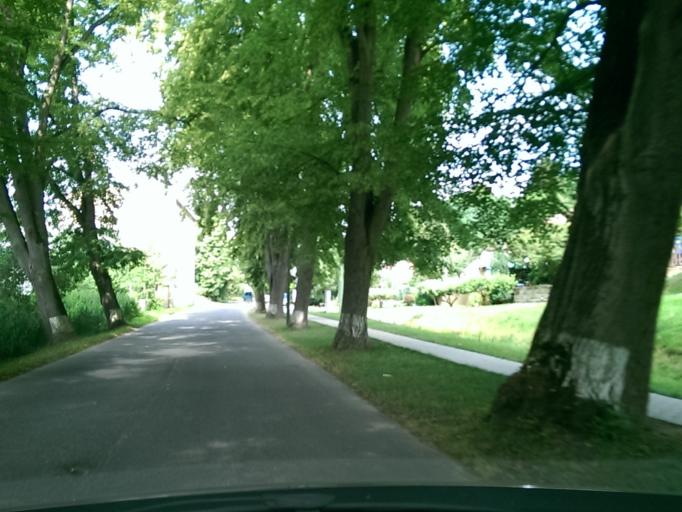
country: CZ
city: Duba
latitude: 50.5374
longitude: 14.5518
